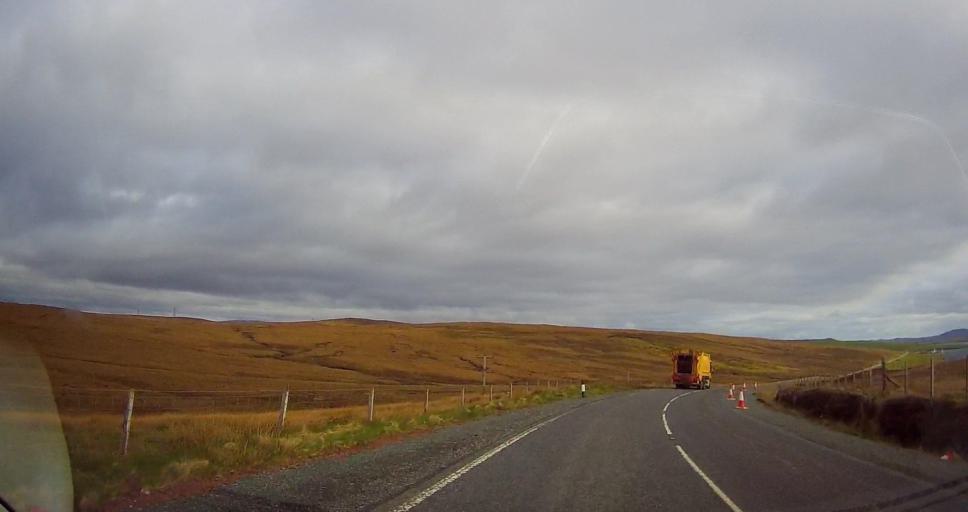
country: GB
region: Scotland
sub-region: Shetland Islands
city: Lerwick
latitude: 60.4494
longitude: -1.2126
